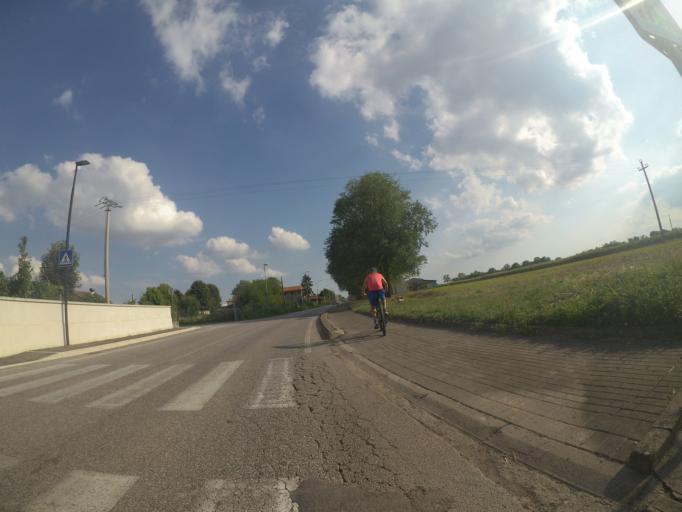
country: IT
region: Friuli Venezia Giulia
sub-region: Provincia di Udine
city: San Vito di Fagagna
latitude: 46.0665
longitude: 13.0828
